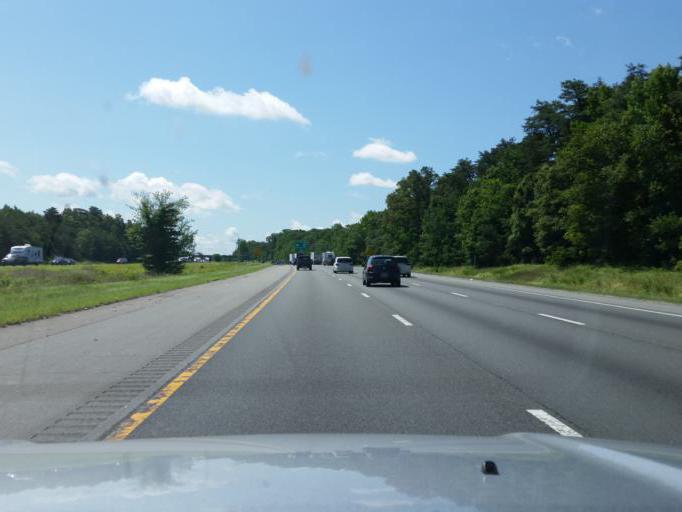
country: US
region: Virginia
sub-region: City of Fredericksburg
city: Fredericksburg
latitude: 38.2566
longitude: -77.5130
